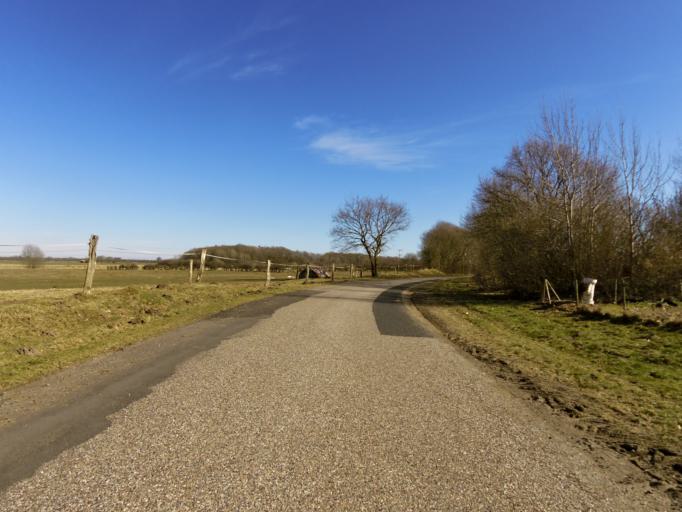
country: DK
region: South Denmark
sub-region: Tonder Kommune
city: Toftlund
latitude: 55.2321
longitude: 9.1307
